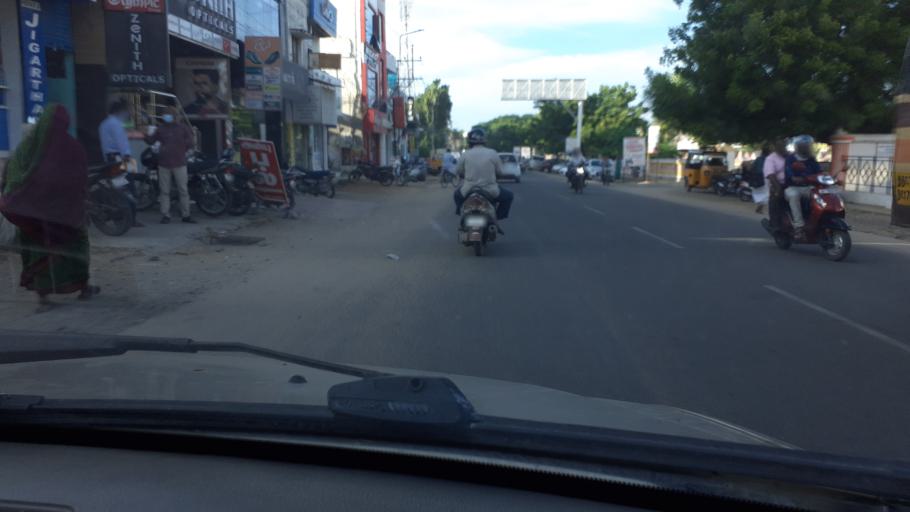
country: IN
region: Tamil Nadu
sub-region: Tirunelveli Kattabo
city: Tirunelveli
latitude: 8.7200
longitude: 77.7323
